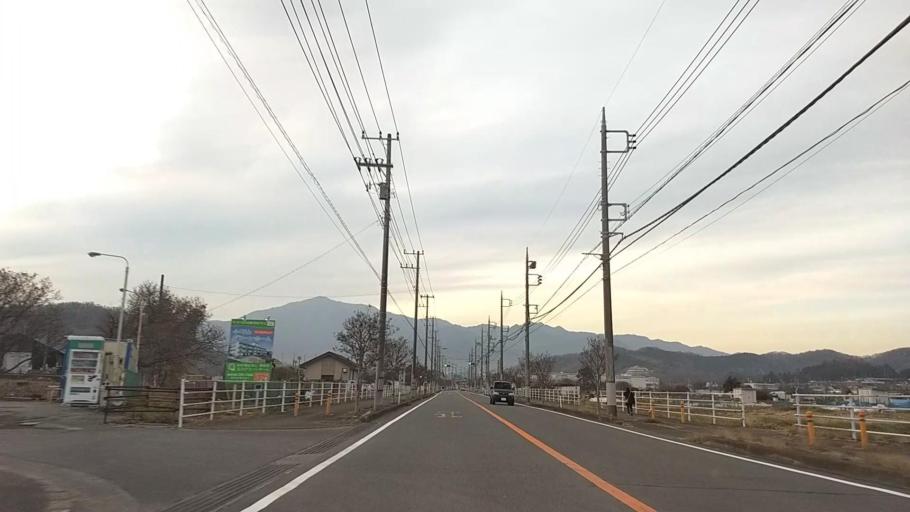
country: JP
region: Kanagawa
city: Atsugi
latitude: 35.4297
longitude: 139.3340
